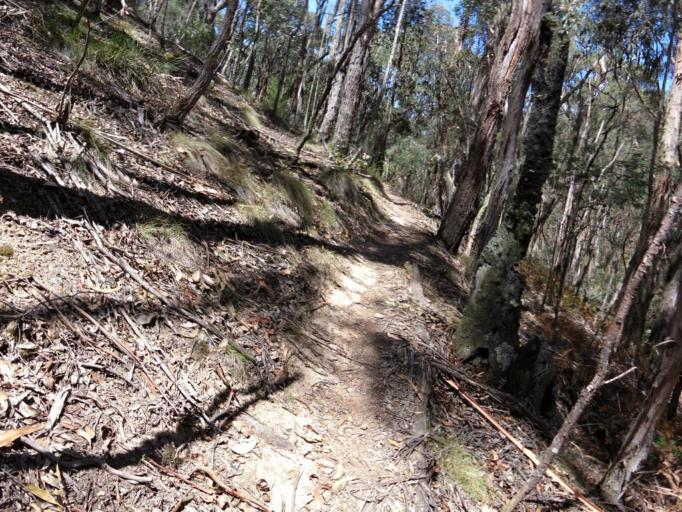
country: AU
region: Victoria
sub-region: Melton
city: Melton West
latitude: -37.4893
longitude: 144.5365
